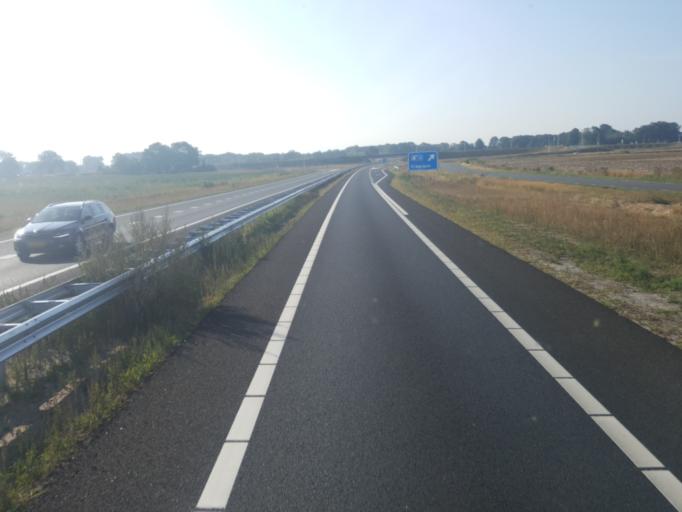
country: NL
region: Gelderland
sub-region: Berkelland
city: Eibergen
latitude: 52.0906
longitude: 6.6268
